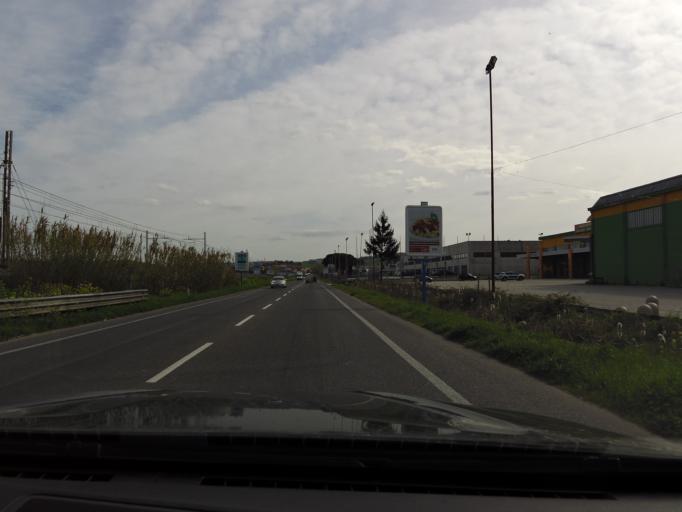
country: IT
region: The Marches
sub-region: Provincia di Ancona
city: Camerano
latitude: 43.5076
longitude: 13.5313
